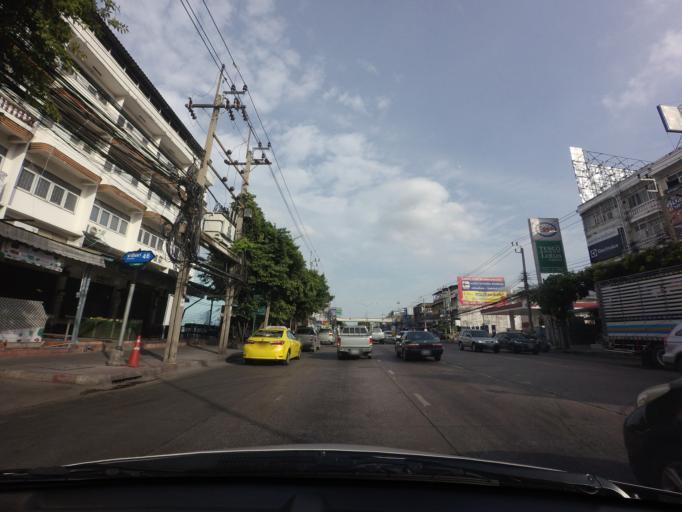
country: TH
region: Bangkok
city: Bueng Kum
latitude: 13.7961
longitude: 100.6509
